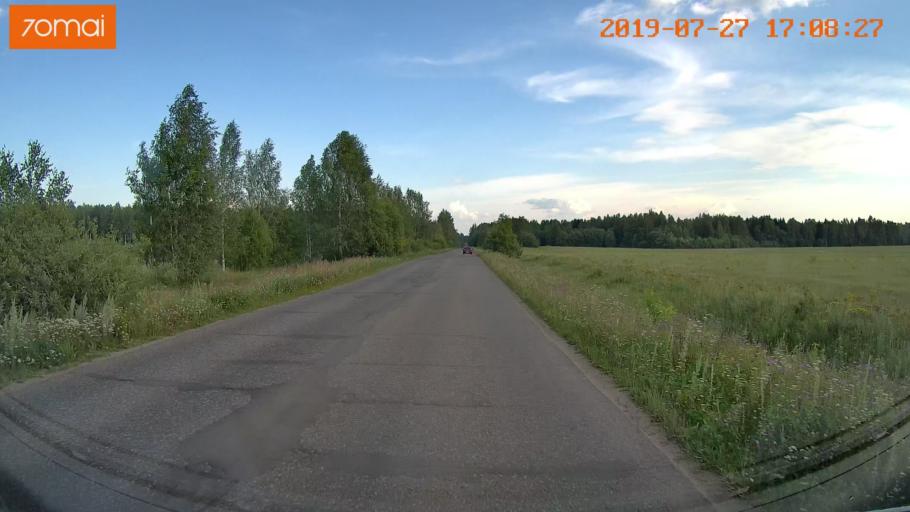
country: RU
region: Ivanovo
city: Novo-Talitsy
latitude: 57.0825
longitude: 40.8377
